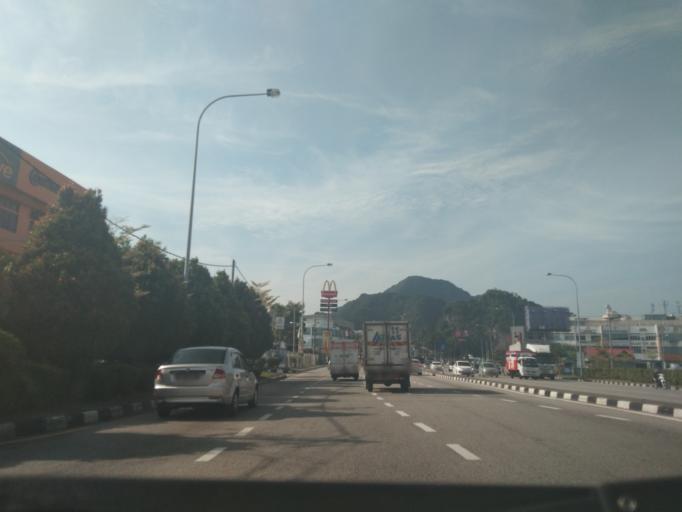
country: MY
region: Perak
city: Ipoh
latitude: 4.5733
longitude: 101.1117
